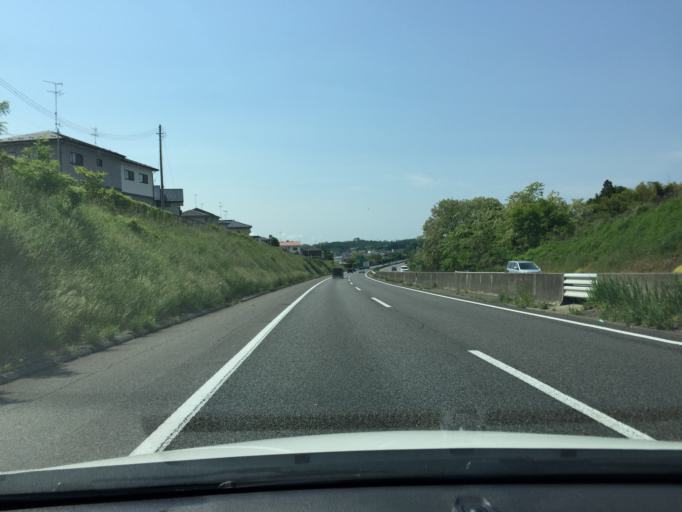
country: JP
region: Fukushima
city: Sukagawa
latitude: 37.2993
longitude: 140.3512
